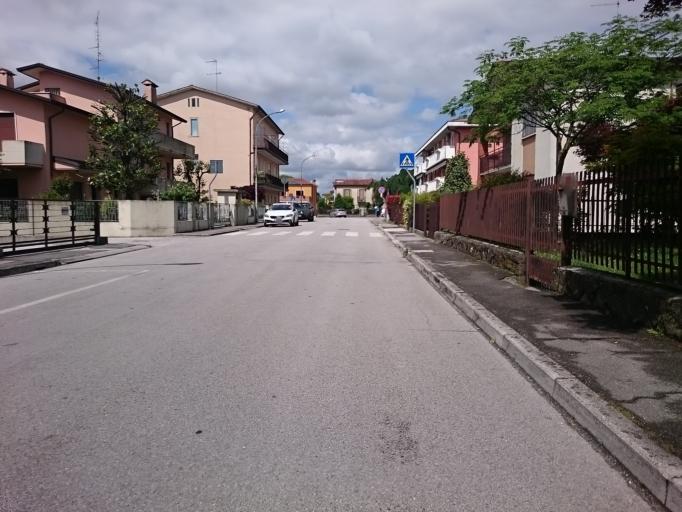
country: IT
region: Veneto
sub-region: Provincia di Padova
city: Mestrino
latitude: 45.4450
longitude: 11.7591
